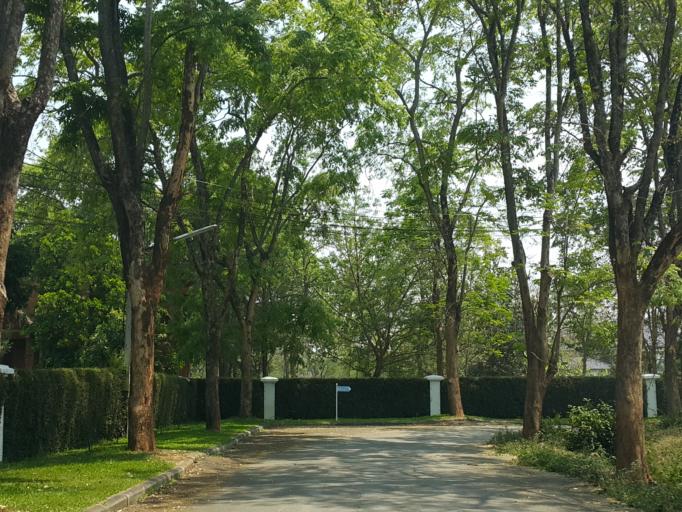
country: TH
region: Chiang Mai
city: Saraphi
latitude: 18.7292
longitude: 98.9759
